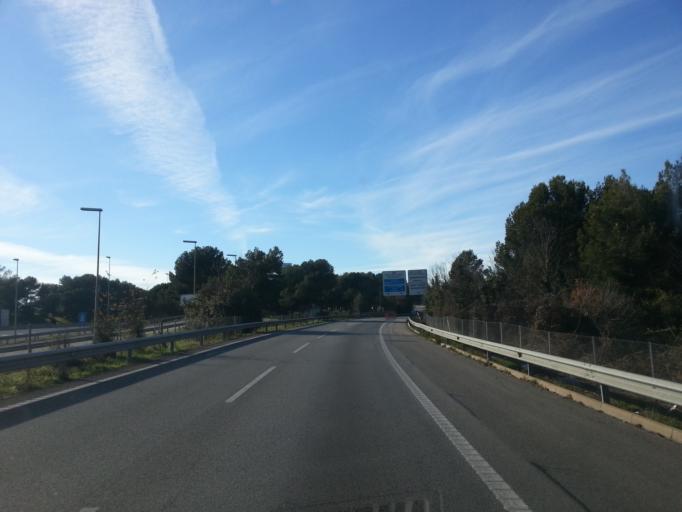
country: ES
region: Catalonia
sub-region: Provincia de Barcelona
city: Barbera del Valles
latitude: 41.4935
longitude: 2.1031
